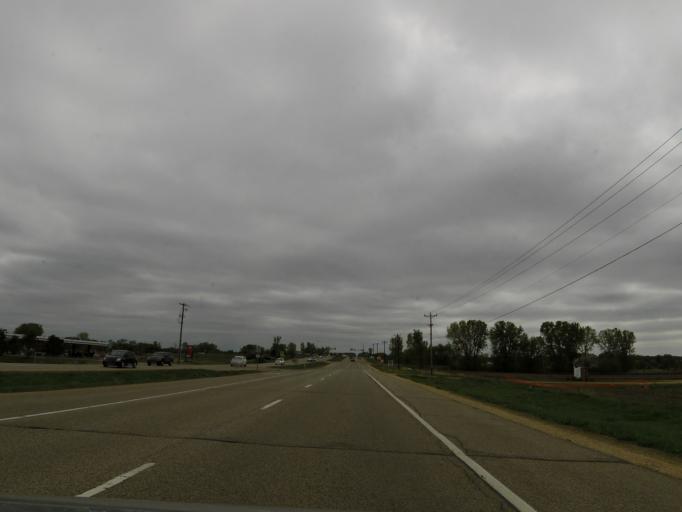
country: US
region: Minnesota
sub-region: Washington County
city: Lake Elmo
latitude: 44.9535
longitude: -92.8628
